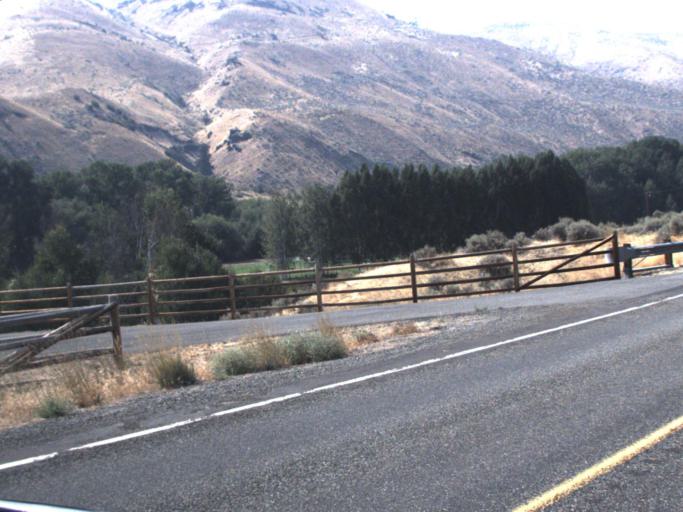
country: US
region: Washington
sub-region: Kittitas County
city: Ellensburg
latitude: 46.9046
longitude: -120.4953
